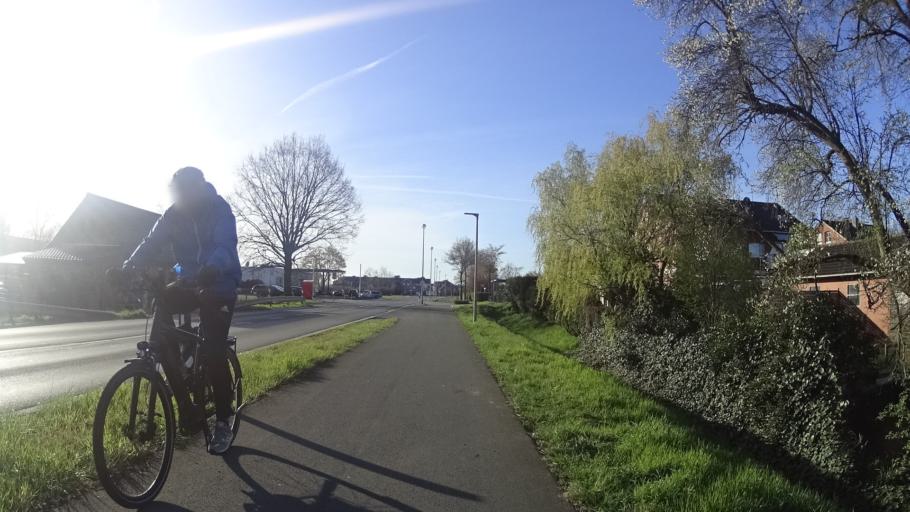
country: DE
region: North Rhine-Westphalia
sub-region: Regierungsbezirk Munster
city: Greven
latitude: 52.1041
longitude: 7.5861
